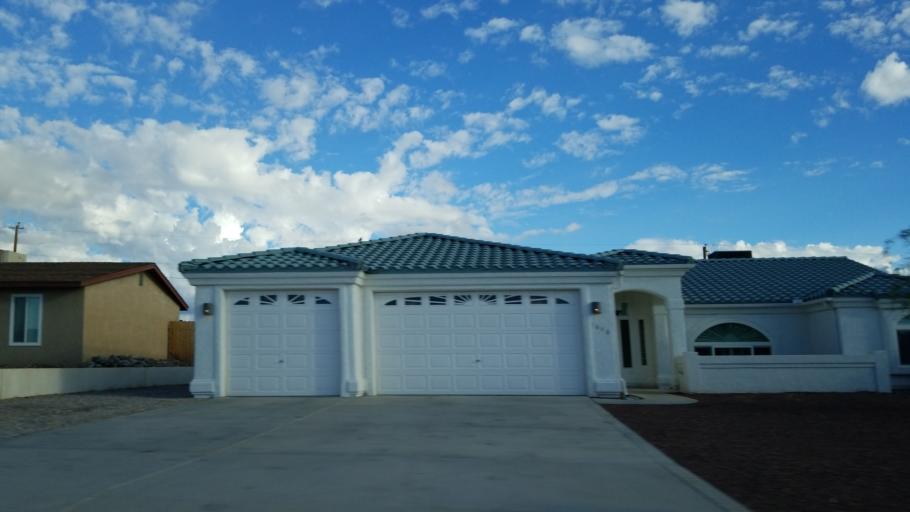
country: US
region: Arizona
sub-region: Mohave County
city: Lake Havasu City
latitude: 34.4566
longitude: -114.2602
